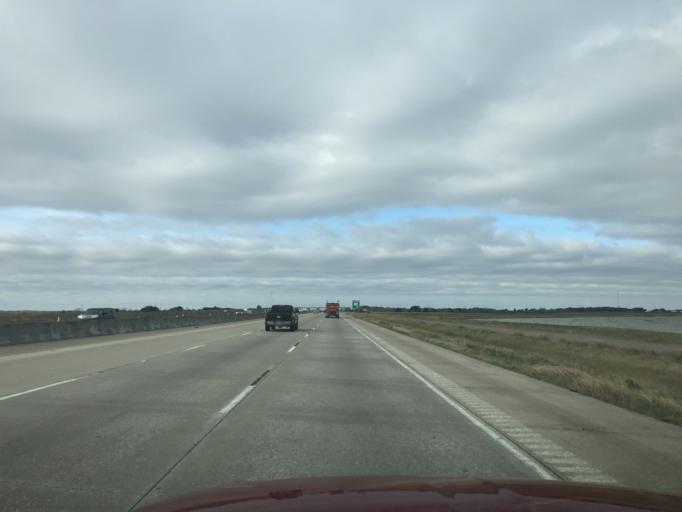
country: US
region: Texas
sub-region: Chambers County
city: Winnie
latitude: 29.8297
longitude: -94.4739
